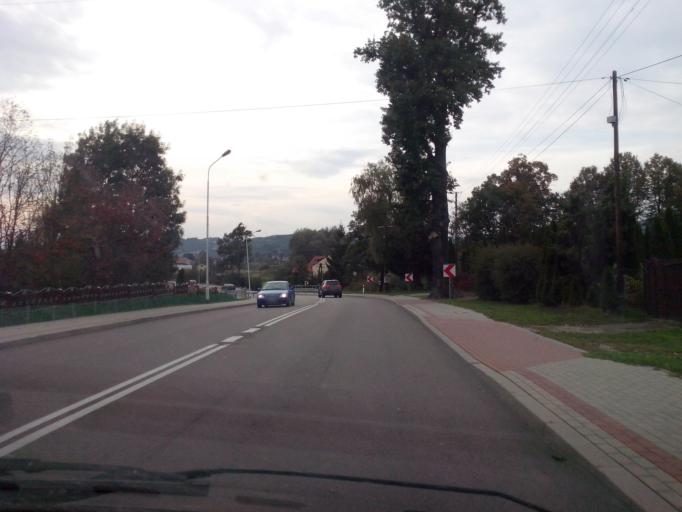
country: PL
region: Subcarpathian Voivodeship
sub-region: Powiat przemyski
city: Dubiecko
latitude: 49.8265
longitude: 22.3891
